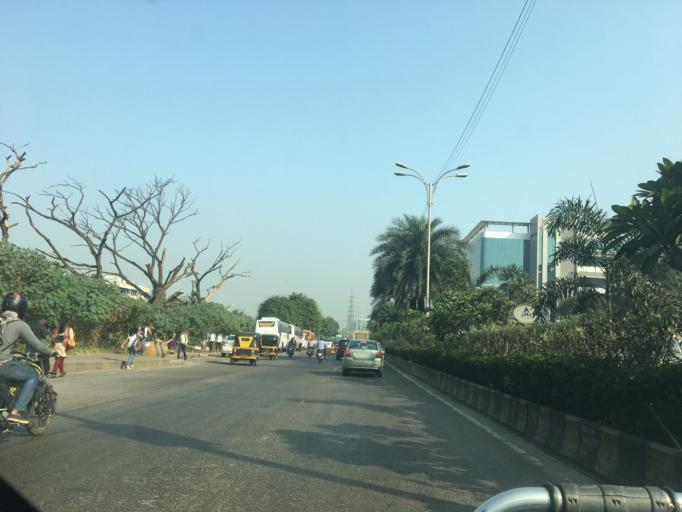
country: IN
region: Maharashtra
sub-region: Thane
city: Airoli
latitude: 19.1608
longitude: 72.9999
